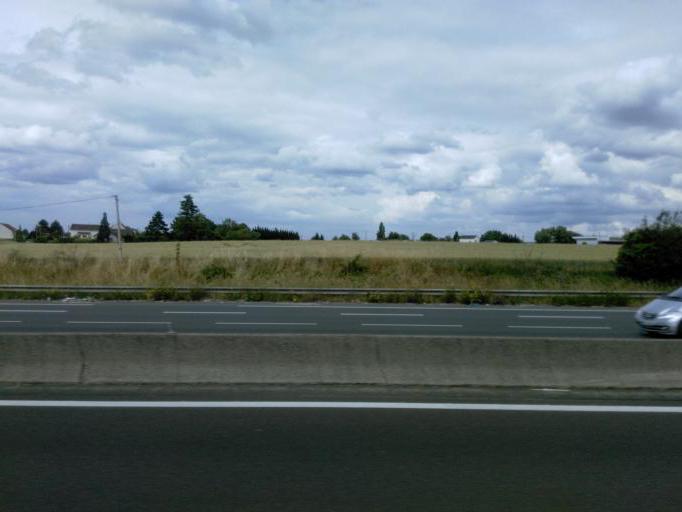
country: FR
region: Ile-de-France
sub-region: Departement du Val-d'Oise
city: Pierrelaye
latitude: 49.0119
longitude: 2.1512
